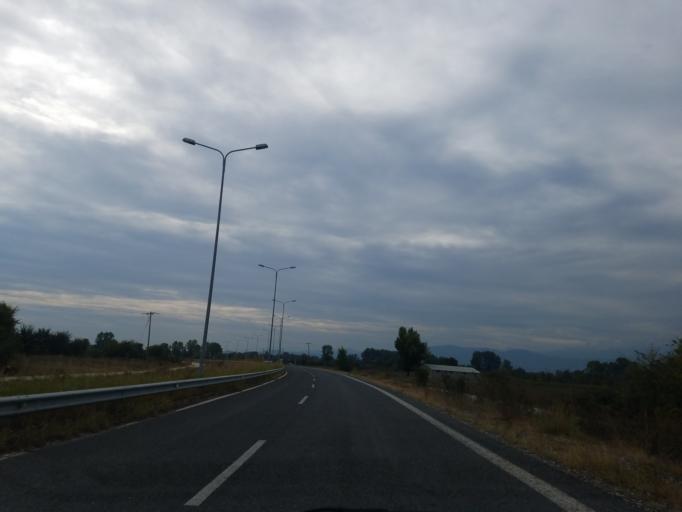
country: GR
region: Thessaly
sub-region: Trikala
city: Pyrgetos
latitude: 39.5387
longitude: 21.7360
